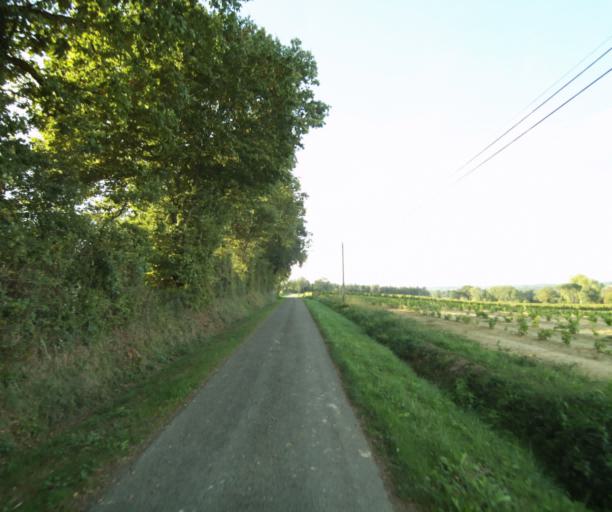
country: FR
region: Midi-Pyrenees
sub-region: Departement du Gers
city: Eauze
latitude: 43.8543
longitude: 0.0136
